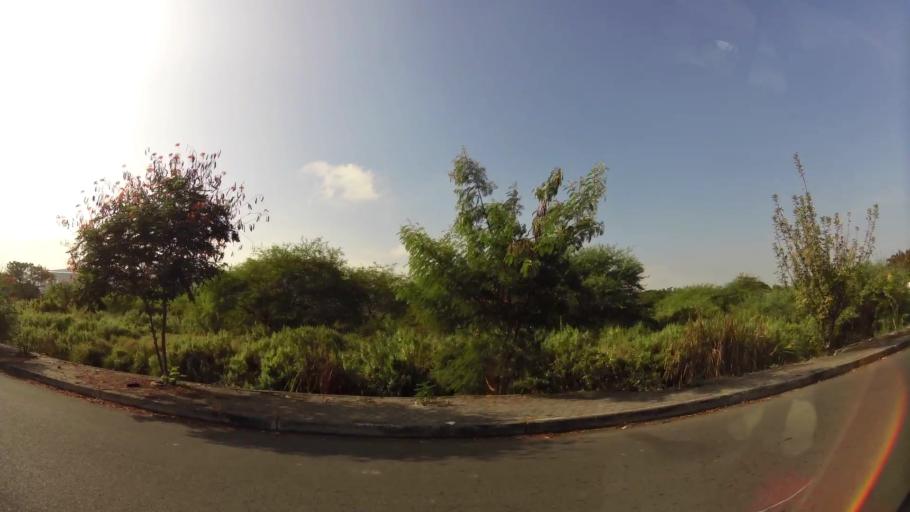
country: EC
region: Guayas
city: Eloy Alfaro
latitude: -2.1999
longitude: -79.8194
